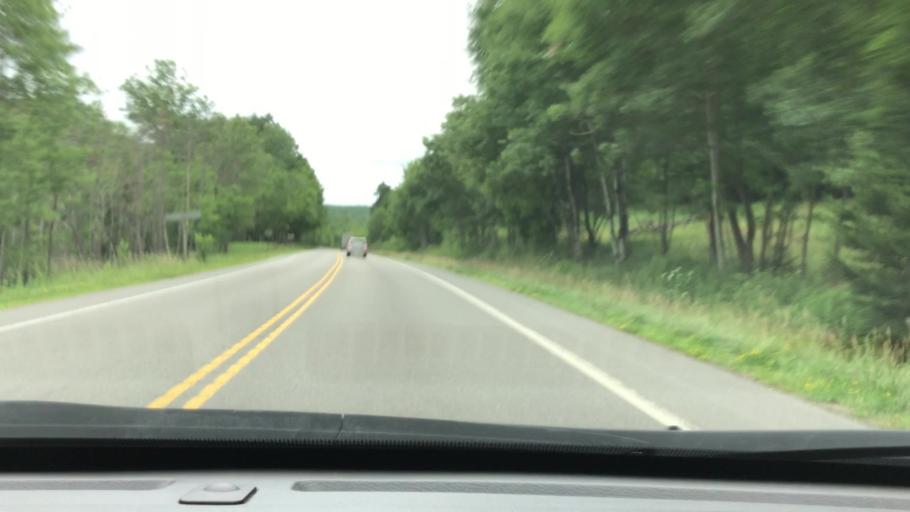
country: US
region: Pennsylvania
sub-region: McKean County
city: Kane
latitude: 41.6734
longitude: -78.6821
